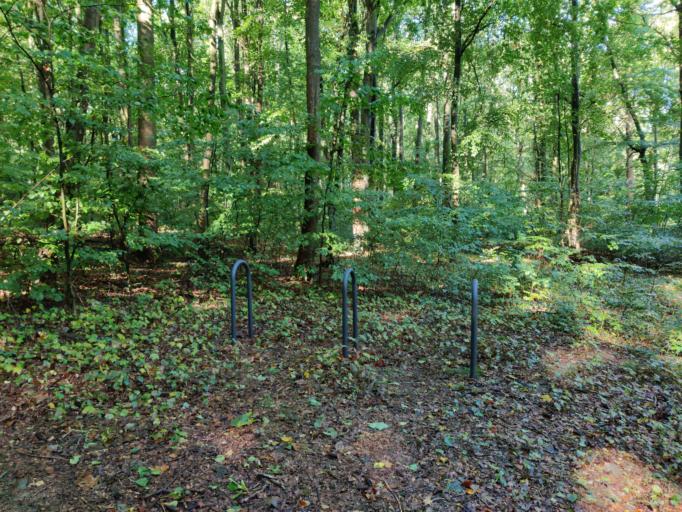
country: DE
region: Mecklenburg-Vorpommern
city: Plau am See
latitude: 53.4184
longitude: 12.2725
